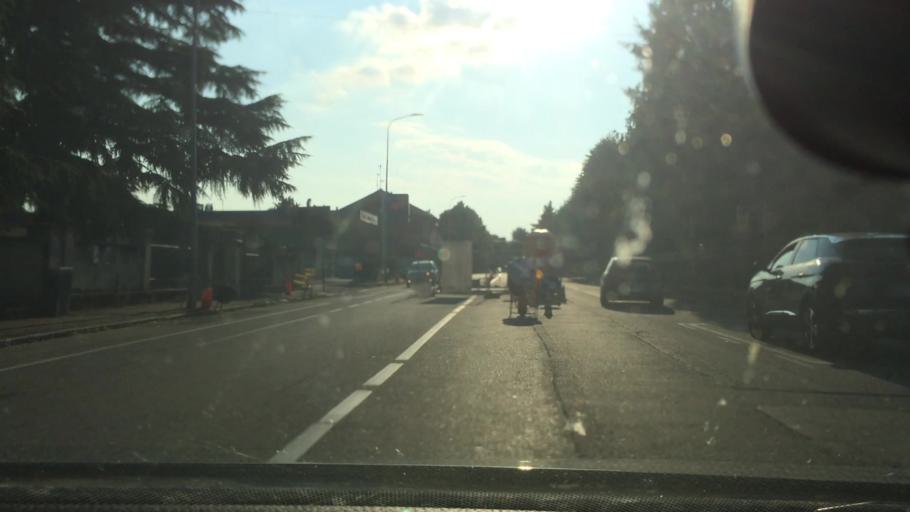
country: IT
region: Lombardy
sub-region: Citta metropolitana di Milano
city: Passirana
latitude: 45.5334
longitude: 9.0330
